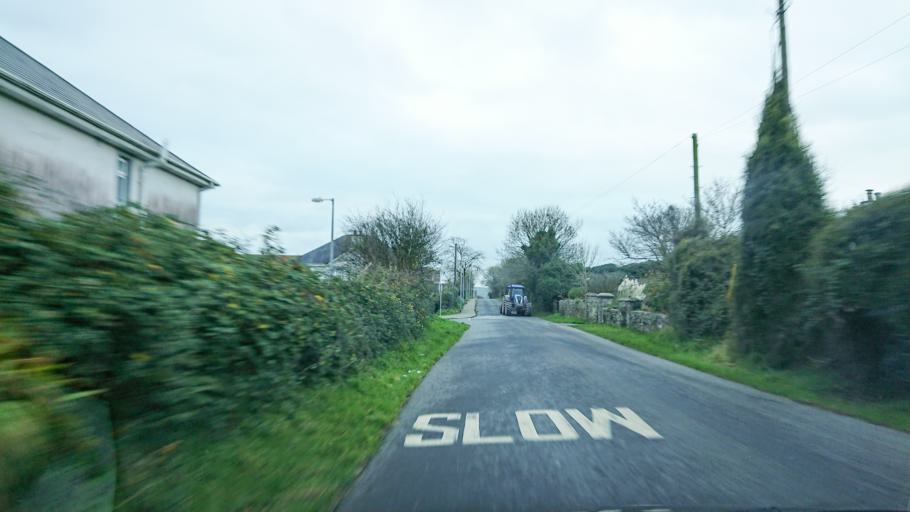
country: IE
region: Munster
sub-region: Waterford
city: Dunmore East
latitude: 52.2320
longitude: -6.9776
